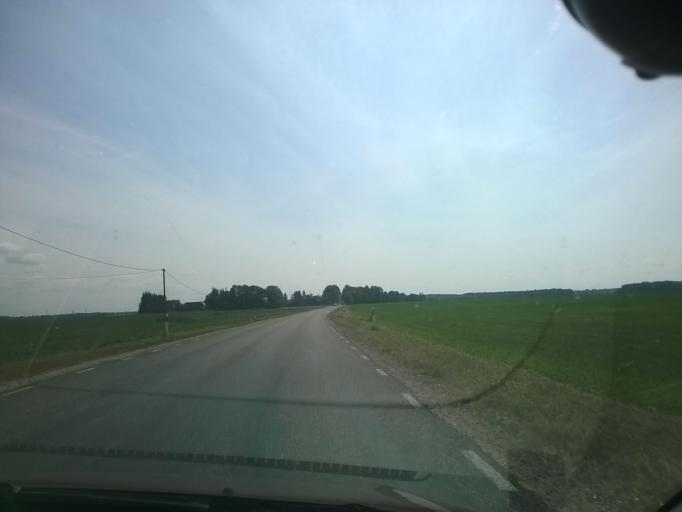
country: EE
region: Tartu
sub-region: Puhja vald
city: Puhja
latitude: 58.2775
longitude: 26.1755
